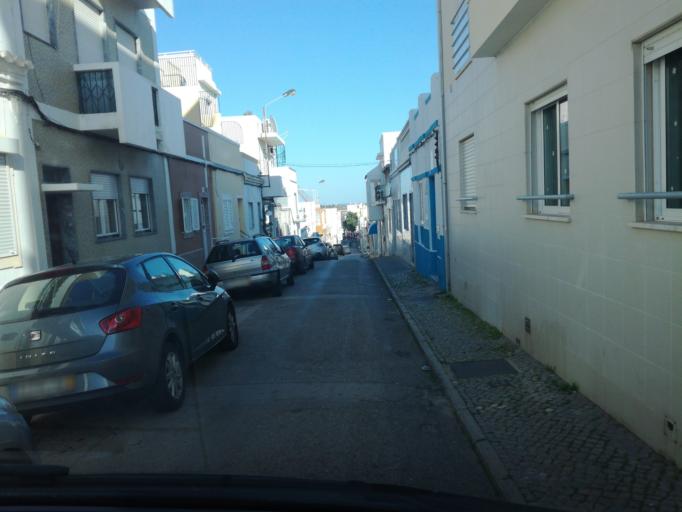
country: PT
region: Faro
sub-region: Olhao
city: Laranjeiro
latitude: 37.0545
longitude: -7.7489
